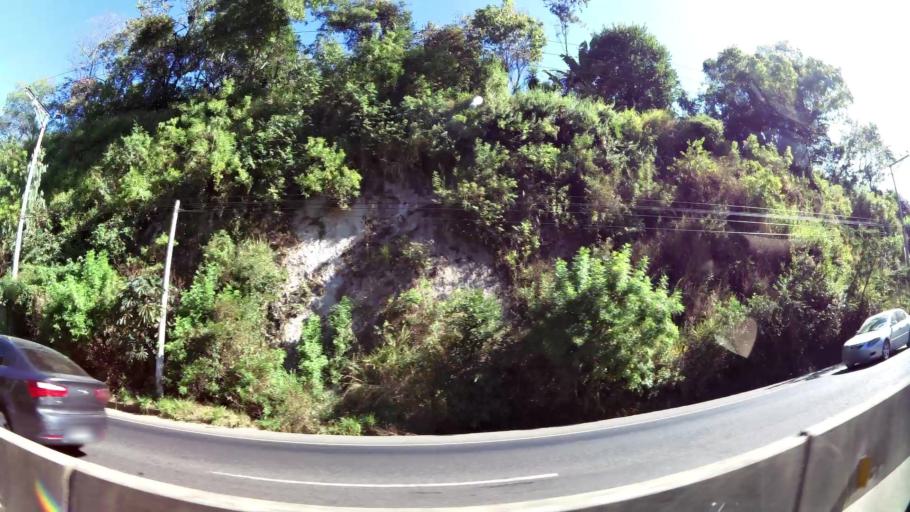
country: SV
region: Santa Ana
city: Santa Ana
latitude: 13.9458
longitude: -89.5561
